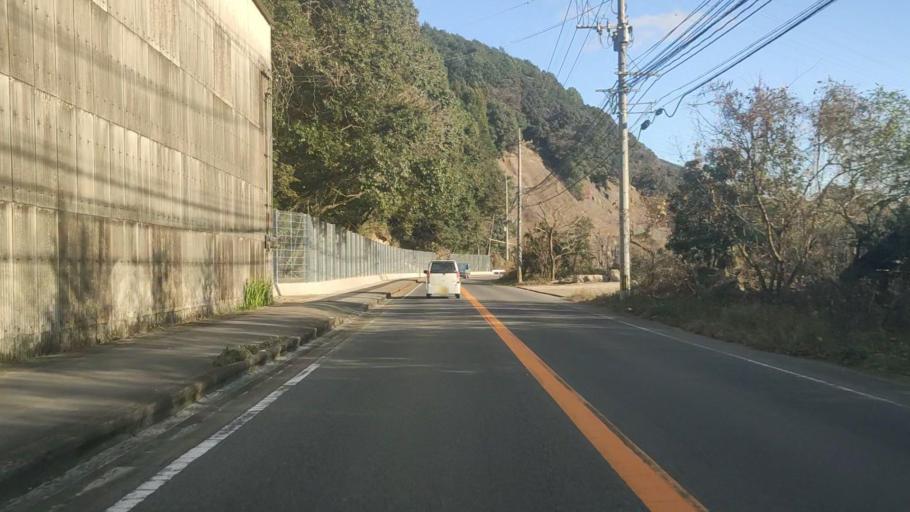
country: JP
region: Saga Prefecture
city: Saga-shi
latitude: 33.3428
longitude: 130.2542
